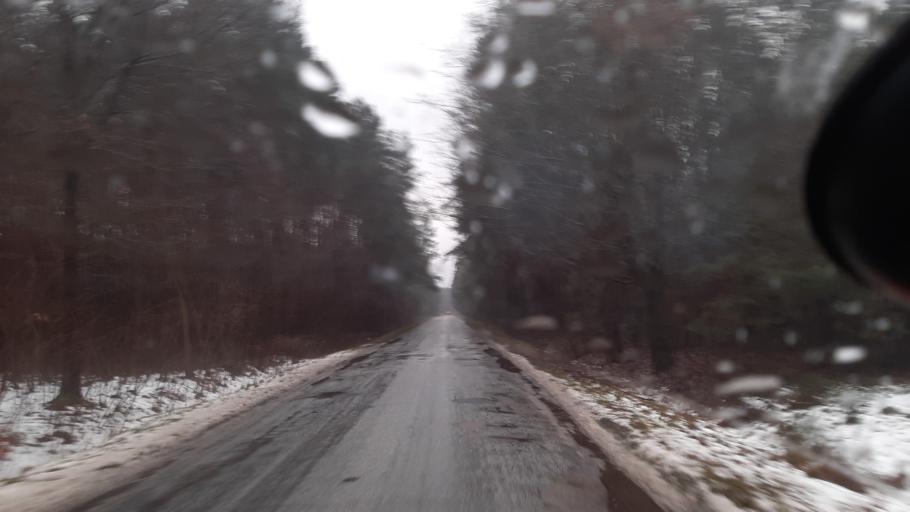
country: PL
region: Lublin Voivodeship
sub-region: Powiat lubartowski
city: Firlej
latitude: 51.5179
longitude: 22.4963
